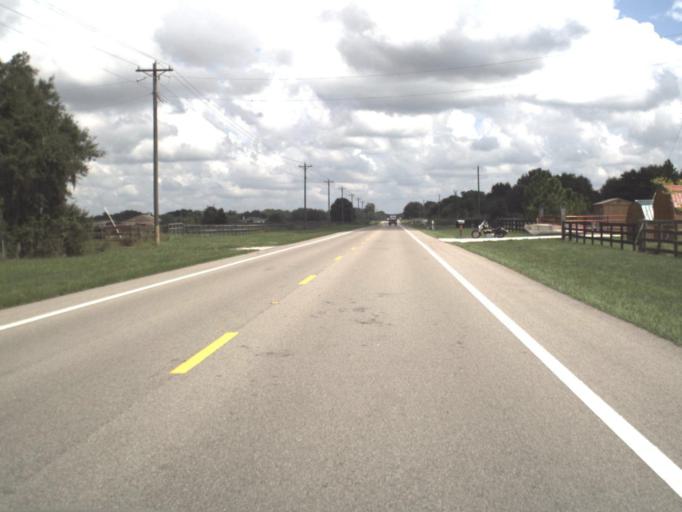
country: US
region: Florida
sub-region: Sarasota County
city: The Meadows
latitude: 27.4767
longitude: -82.2915
